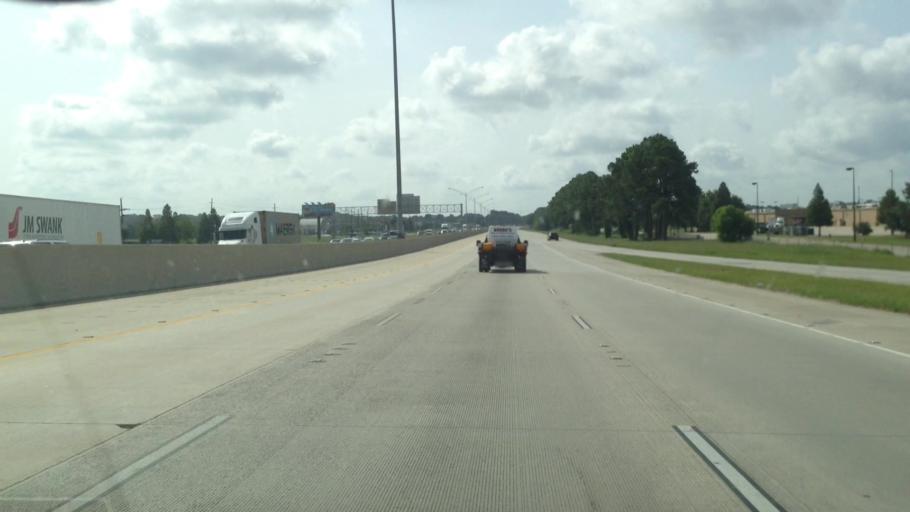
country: US
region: Louisiana
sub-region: East Baton Rouge Parish
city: Village Saint George
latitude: 30.3805
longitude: -91.0634
